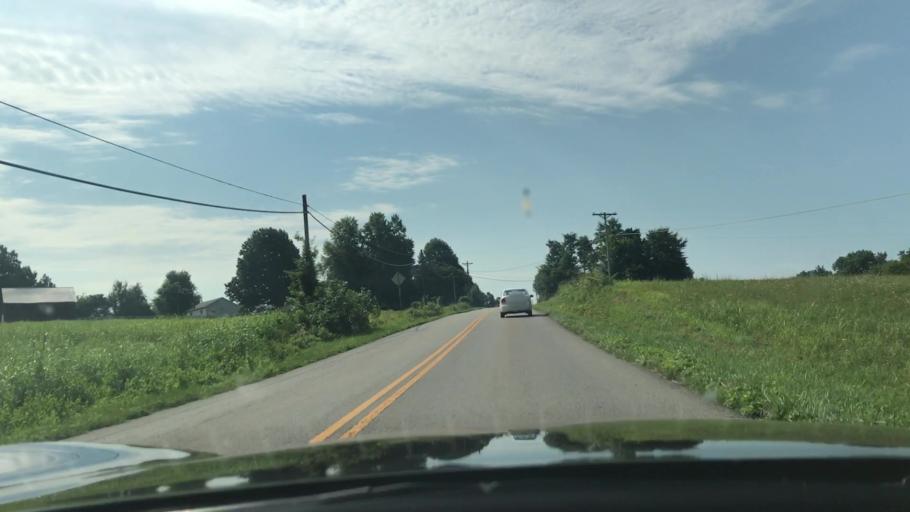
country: US
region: Kentucky
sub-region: Green County
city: Greensburg
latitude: 37.2661
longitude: -85.5625
